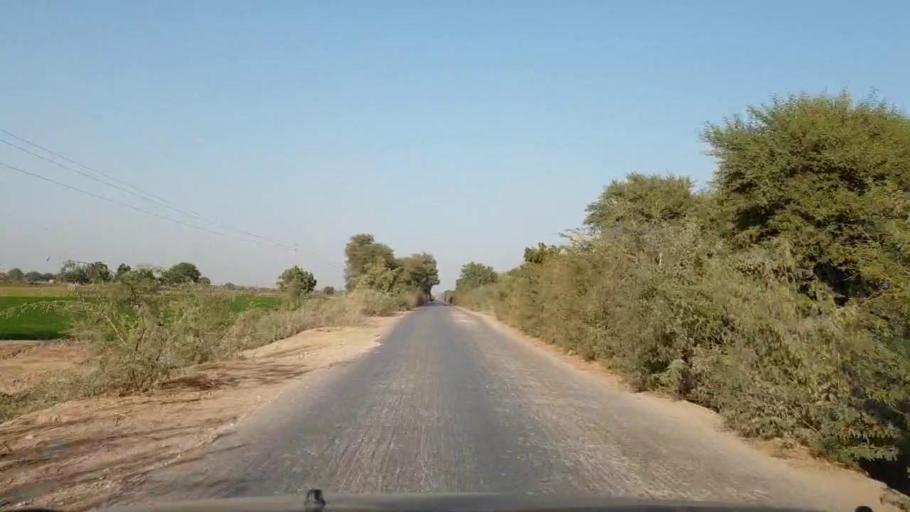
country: PK
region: Sindh
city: Chambar
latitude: 25.2693
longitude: 68.8024
